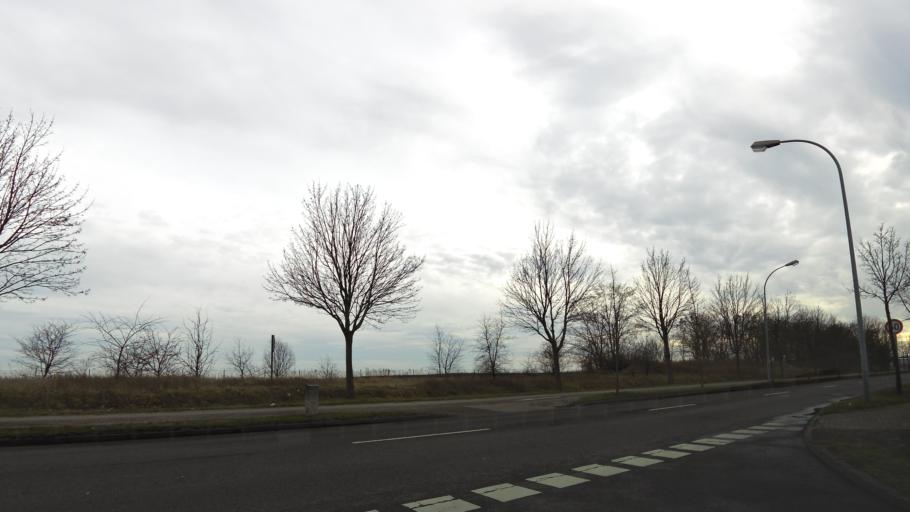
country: DE
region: Brandenburg
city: Strausberg
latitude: 52.5853
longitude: 13.9093
